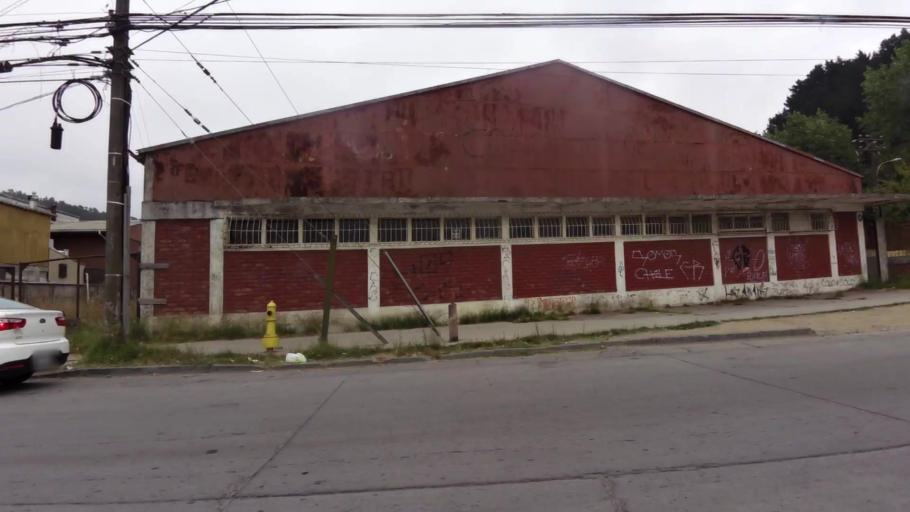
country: CL
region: Biobio
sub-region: Provincia de Concepcion
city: Concepcion
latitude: -36.8226
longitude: -72.9954
